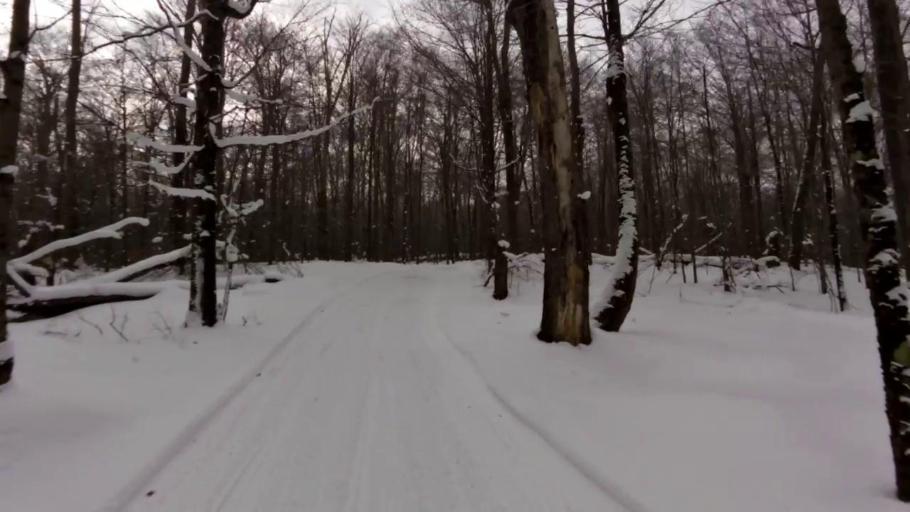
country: US
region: Pennsylvania
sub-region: McKean County
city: Bradford
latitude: 42.0266
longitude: -78.7371
